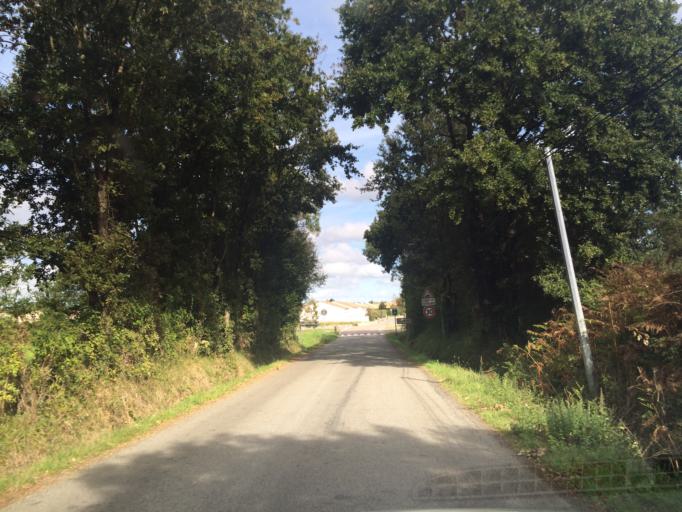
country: FR
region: Pays de la Loire
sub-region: Departement de la Loire-Atlantique
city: Chemere
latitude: 47.1119
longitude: -1.9172
